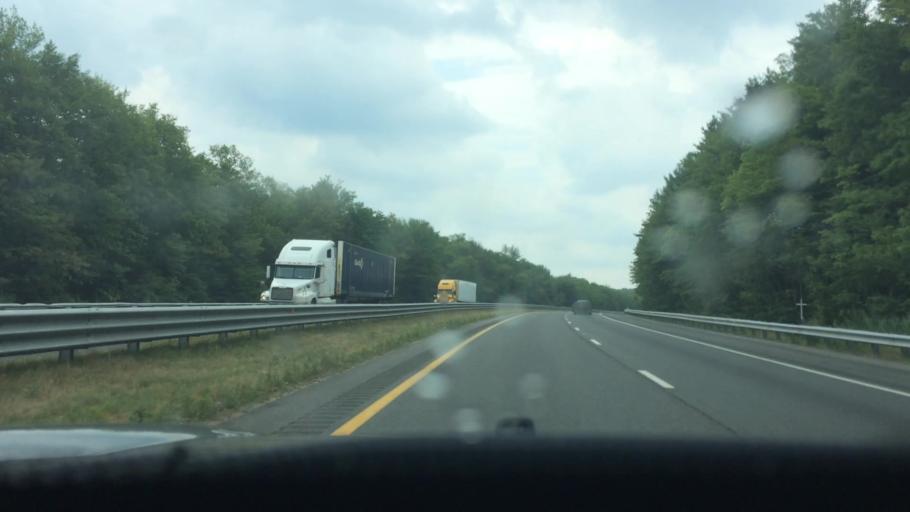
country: US
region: Massachusetts
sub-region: Hampden County
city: Palmer
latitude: 42.1768
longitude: -72.3110
